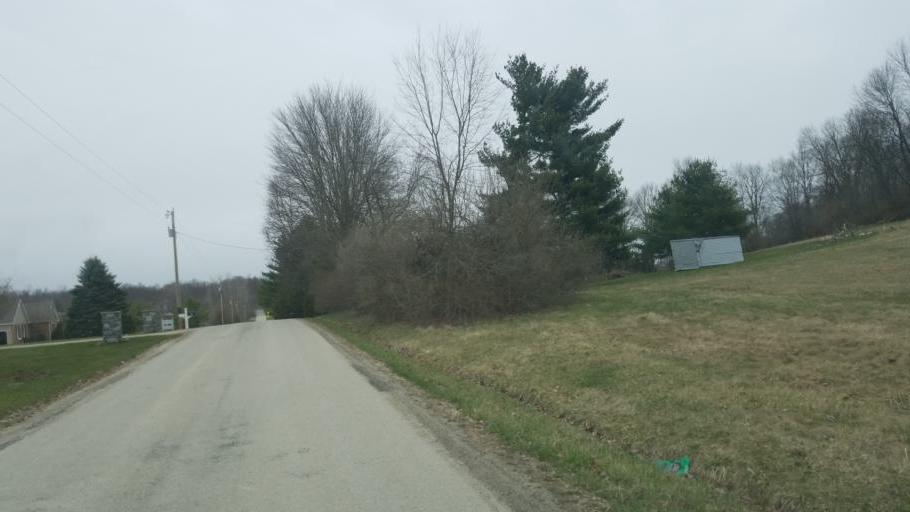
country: US
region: Ohio
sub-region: Knox County
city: Centerburg
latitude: 40.3334
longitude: -82.6474
